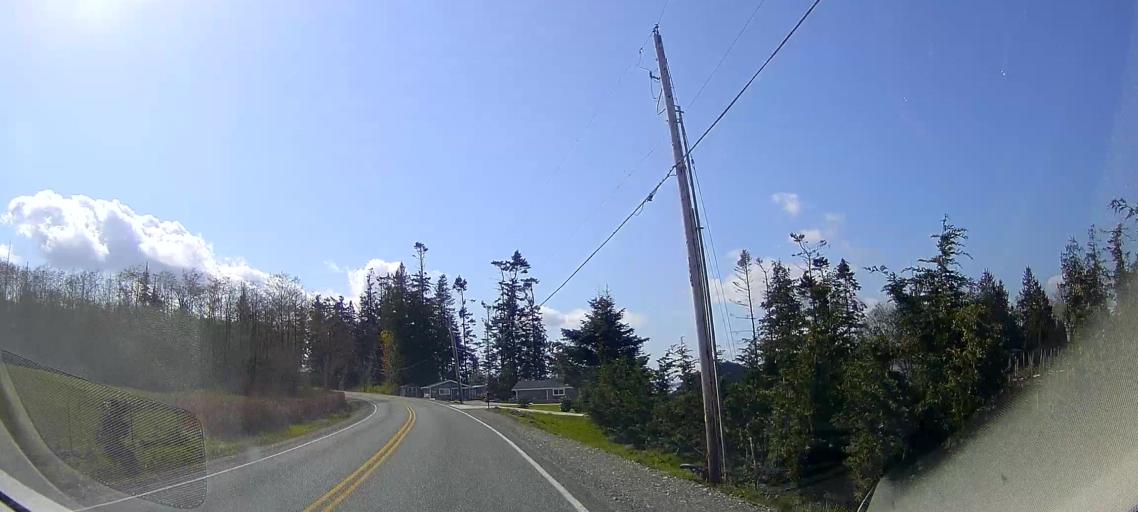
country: US
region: Washington
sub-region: Skagit County
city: Anacortes
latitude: 48.5154
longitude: -122.4781
